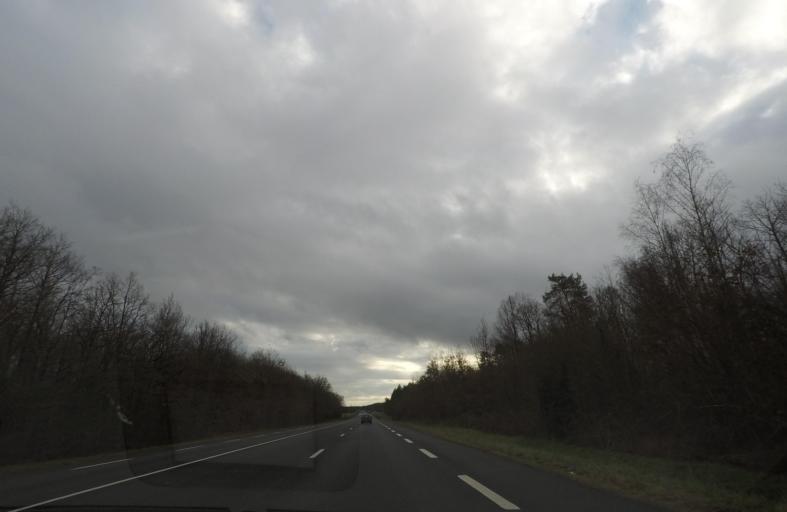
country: FR
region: Centre
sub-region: Departement du Loir-et-Cher
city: Soings-en-Sologne
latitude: 47.4515
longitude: 1.5333
